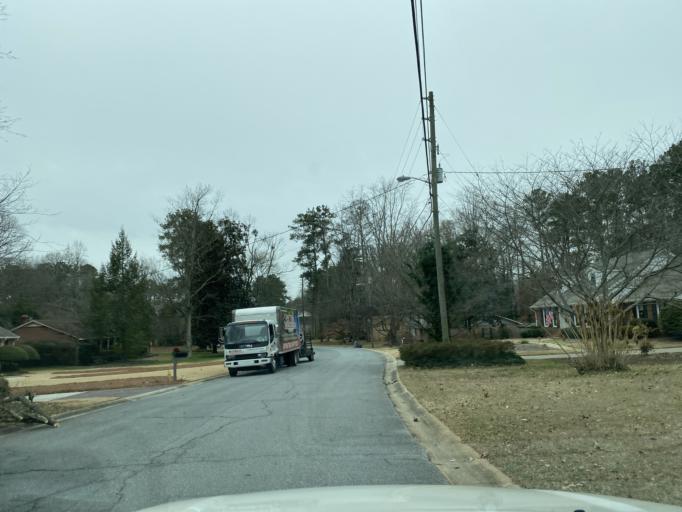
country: US
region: Georgia
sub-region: Cobb County
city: Fair Oaks
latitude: 33.9217
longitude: -84.5698
